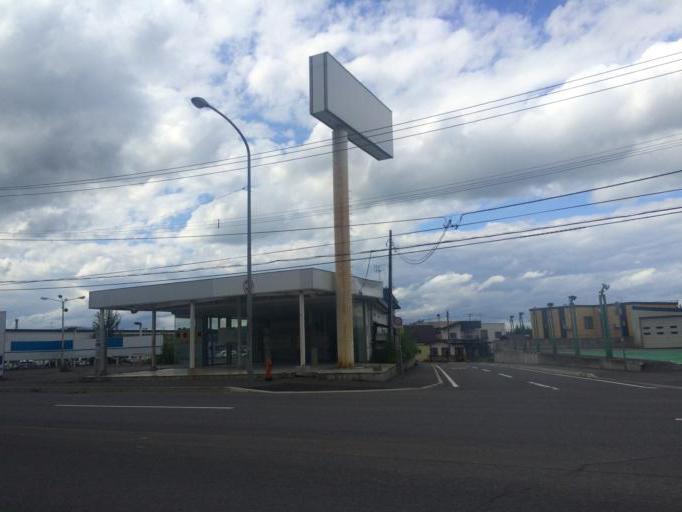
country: JP
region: Hokkaido
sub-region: Asahikawa-shi
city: Asahikawa
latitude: 43.7683
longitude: 142.3197
